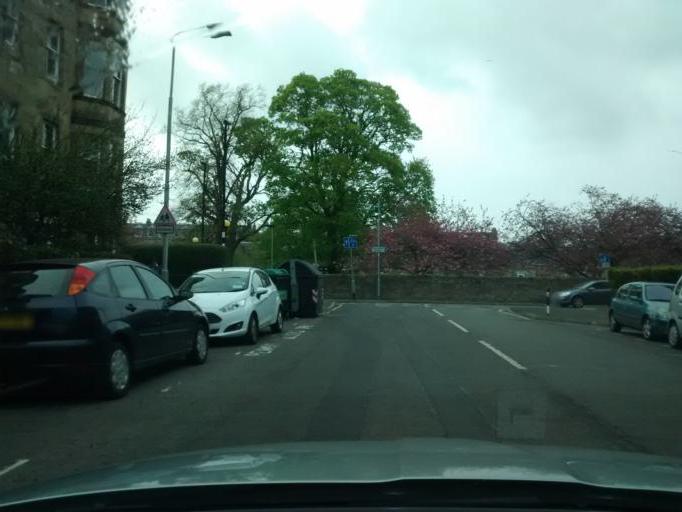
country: GB
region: Scotland
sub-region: Edinburgh
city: Edinburgh
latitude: 55.9278
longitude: -3.2043
